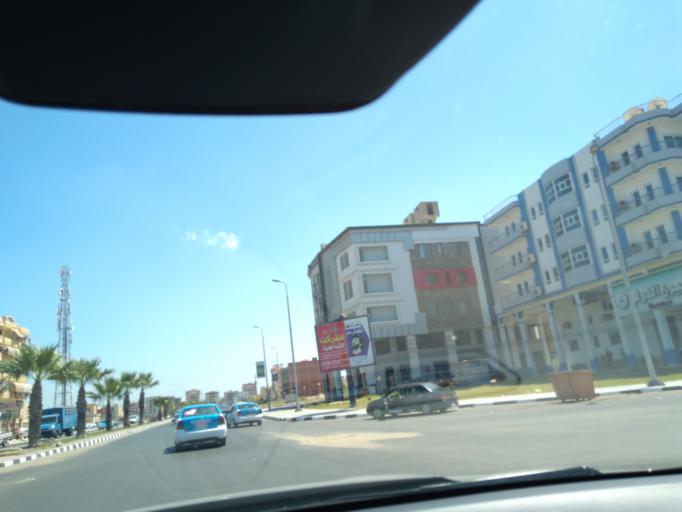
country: EG
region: Dumyat
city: Faraskur
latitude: 31.4393
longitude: 31.6736
